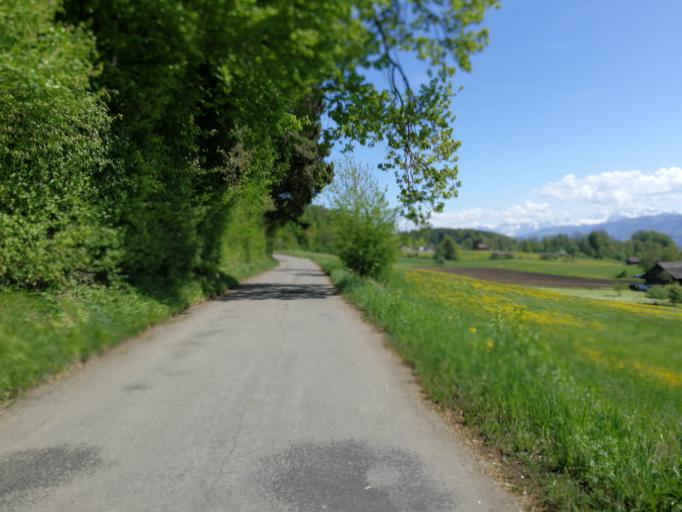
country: CH
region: Zurich
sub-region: Bezirk Meilen
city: Mannedorf
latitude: 47.2656
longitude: 8.6999
